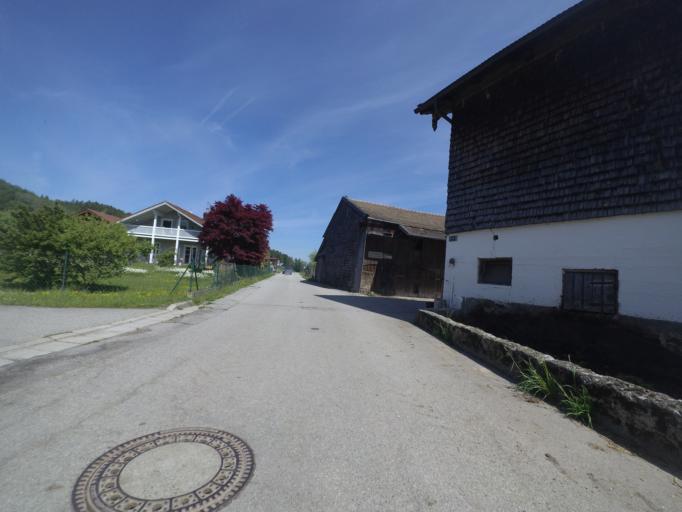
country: DE
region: Bavaria
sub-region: Upper Bavaria
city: Petting
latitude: 47.8951
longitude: 12.8196
